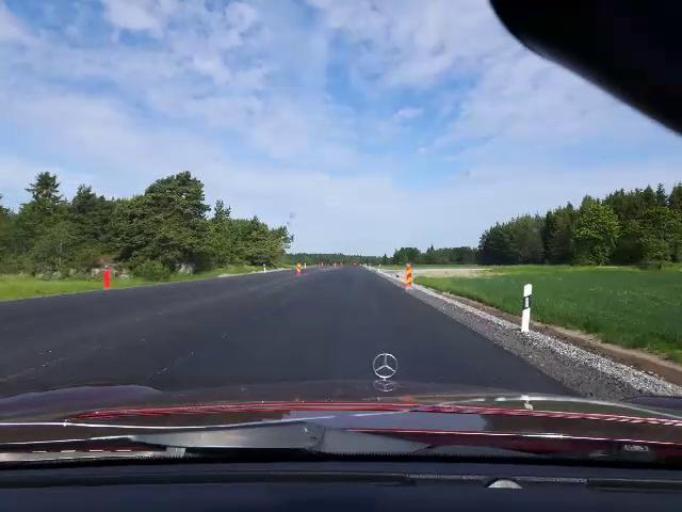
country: SE
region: Uppsala
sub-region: Enkopings Kommun
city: Irsta
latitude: 59.7556
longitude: 16.9346
